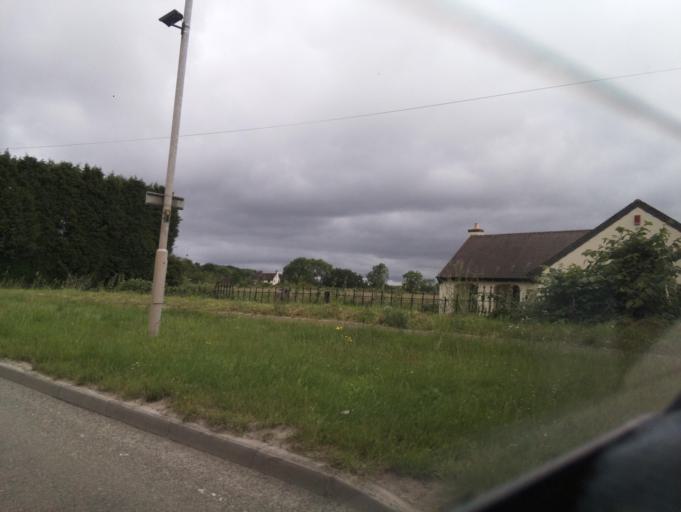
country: GB
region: England
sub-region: Leicestershire
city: Ashby de la Zouch
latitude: 52.7675
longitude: -1.5046
